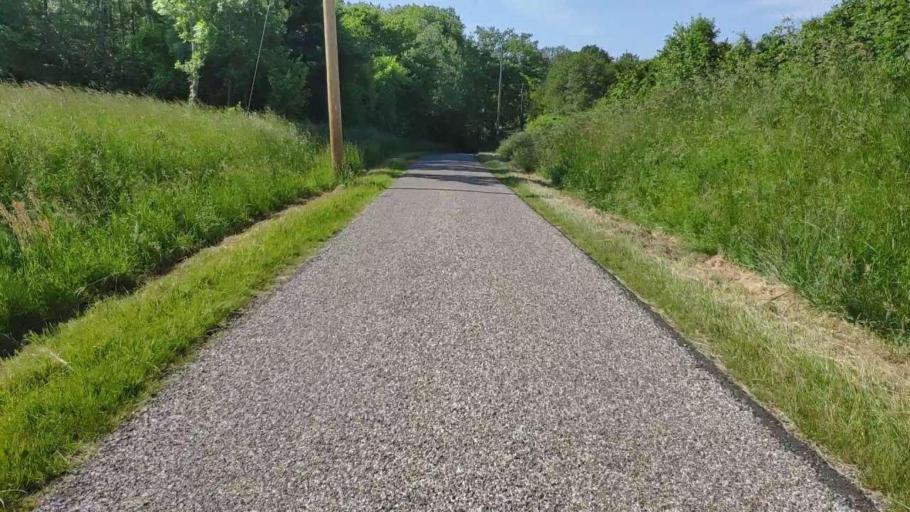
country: FR
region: Franche-Comte
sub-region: Departement du Jura
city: Bletterans
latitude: 46.7020
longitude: 5.4708
